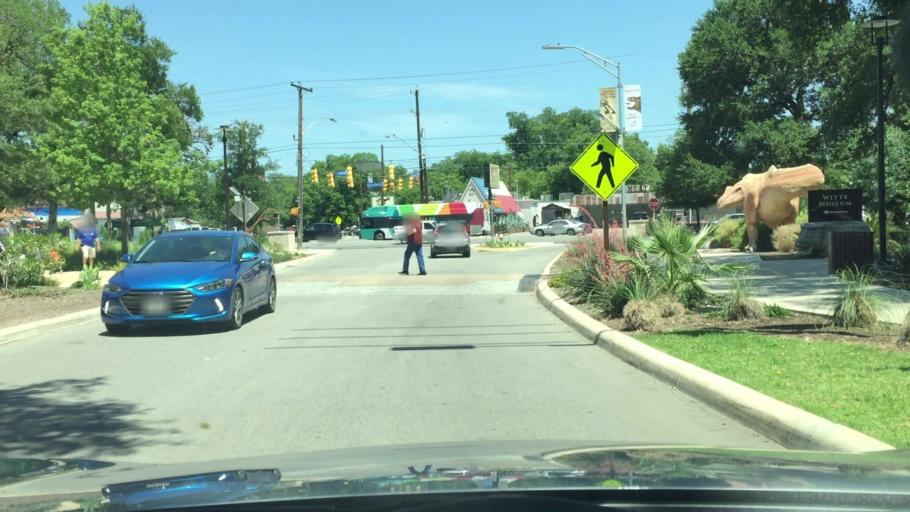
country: US
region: Texas
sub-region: Bexar County
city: Terrell Hills
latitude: 29.4614
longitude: -98.4676
